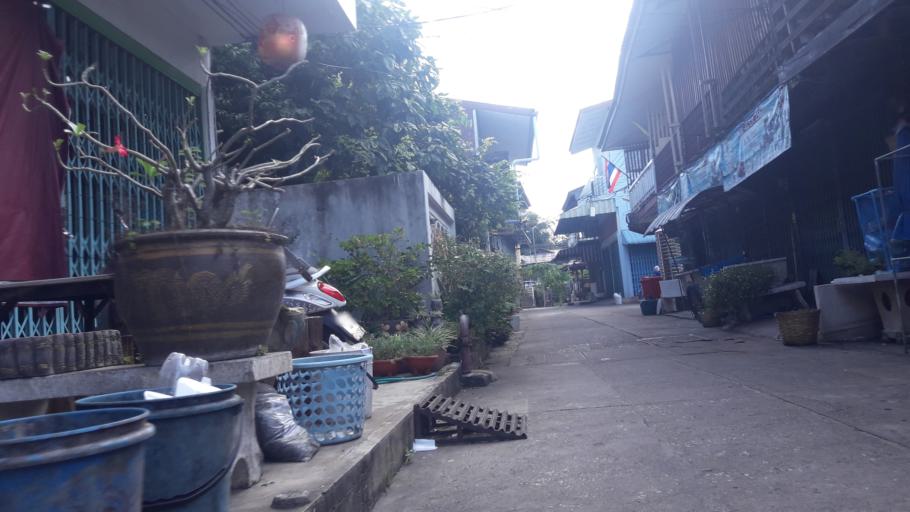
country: TH
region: Phichit
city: Thap Khlo
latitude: 16.1690
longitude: 100.5779
